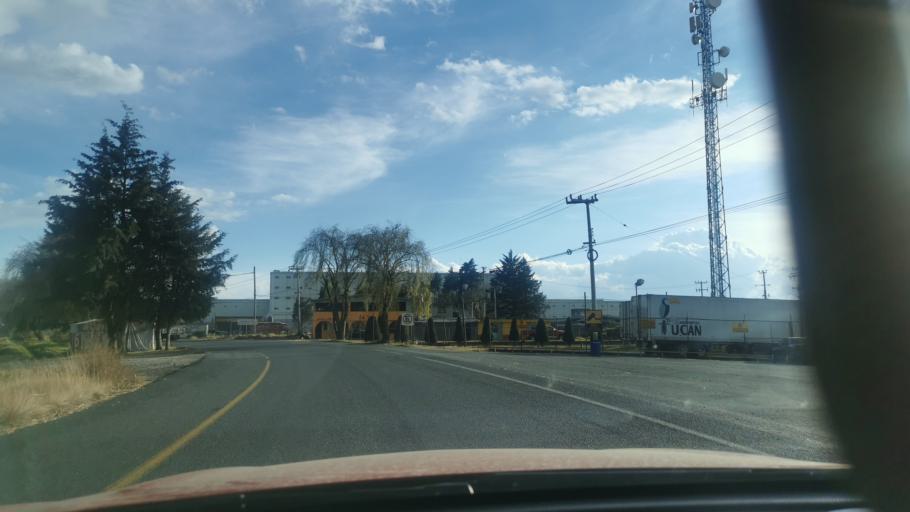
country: MX
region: Mexico
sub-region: Toluca
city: Colonia Aviacion Autopan
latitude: 19.3850
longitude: -99.7086
